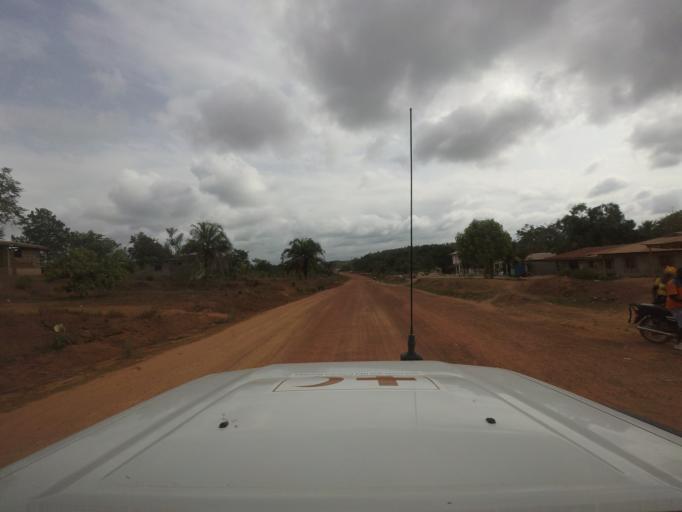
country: LR
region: Bong
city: Gbarnga
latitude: 7.0168
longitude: -9.4744
